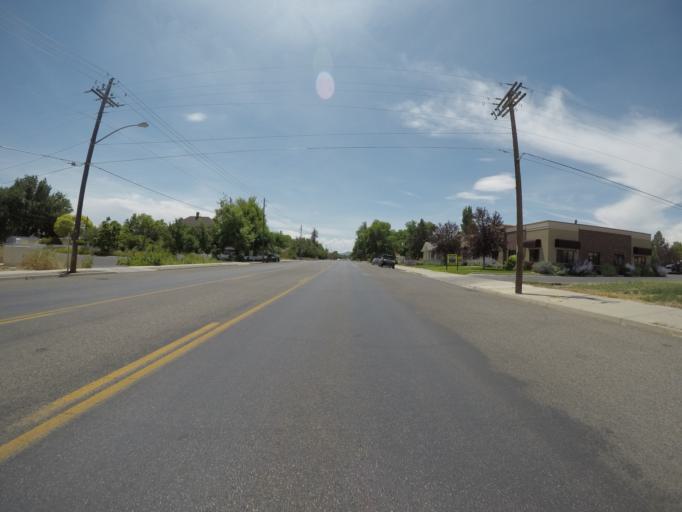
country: US
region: Utah
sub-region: Uintah County
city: Vernal
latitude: 40.4537
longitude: -109.5285
